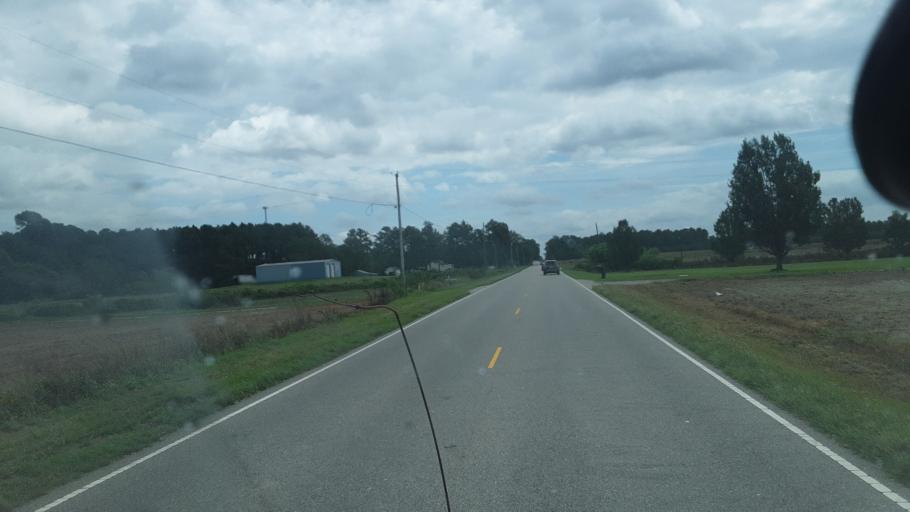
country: US
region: North Carolina
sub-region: Robeson County
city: Maxton
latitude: 34.6810
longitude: -79.4263
